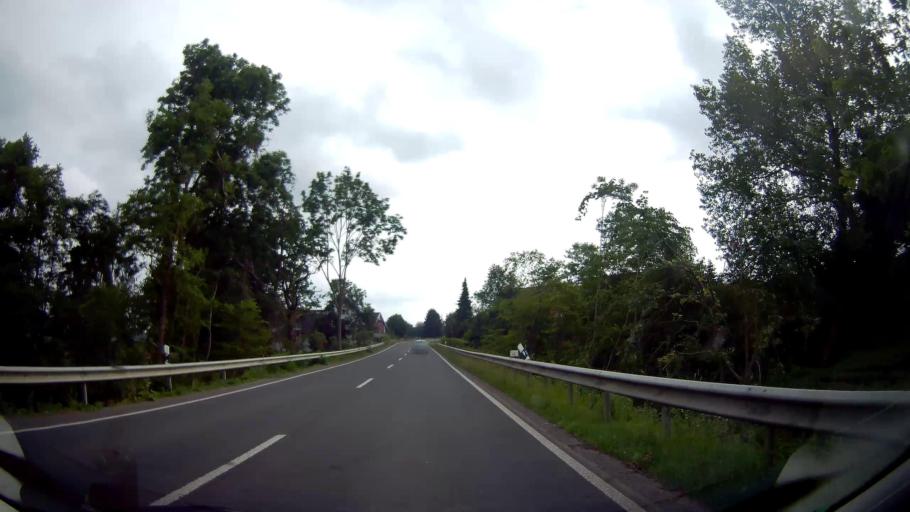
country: DE
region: North Rhine-Westphalia
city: Loehne
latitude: 52.1533
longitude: 8.7217
